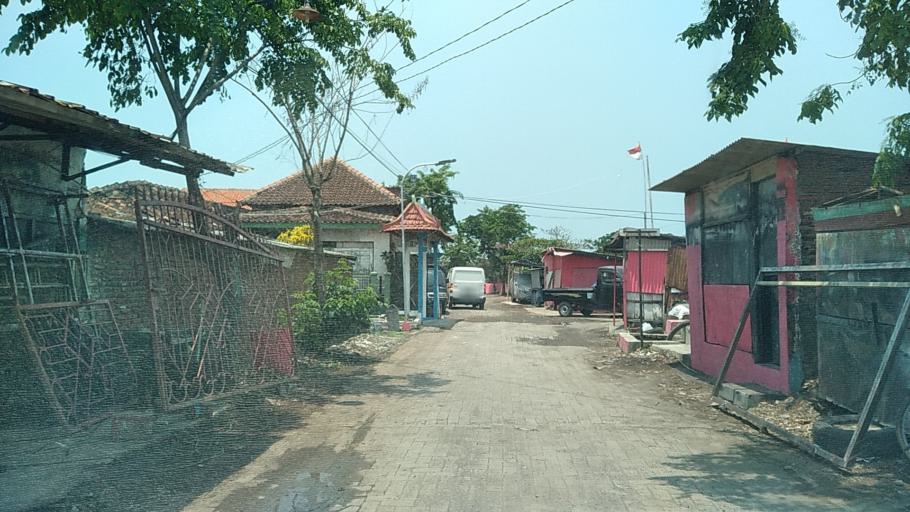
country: ID
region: Central Java
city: Semarang
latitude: -6.9594
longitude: 110.4407
